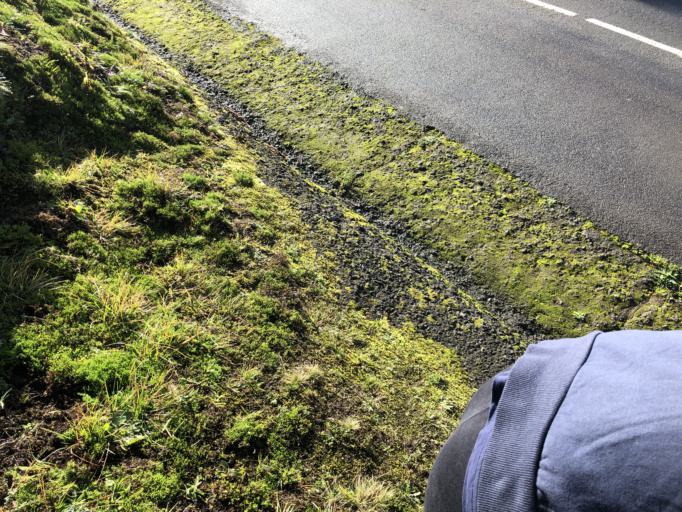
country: PT
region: Azores
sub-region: Ponta Delgada
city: Arrifes
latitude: 37.8359
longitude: -25.7624
